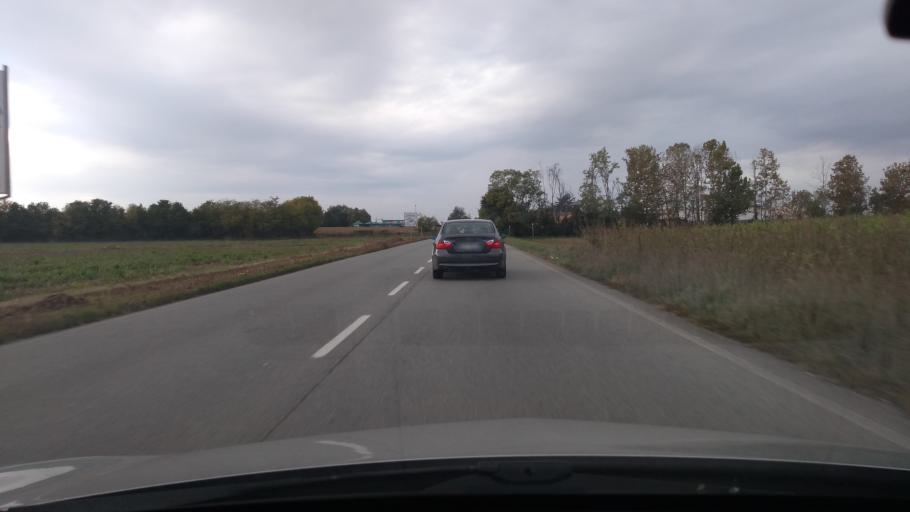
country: IT
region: Lombardy
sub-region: Provincia di Bergamo
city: Spirano
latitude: 45.5929
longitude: 9.6763
